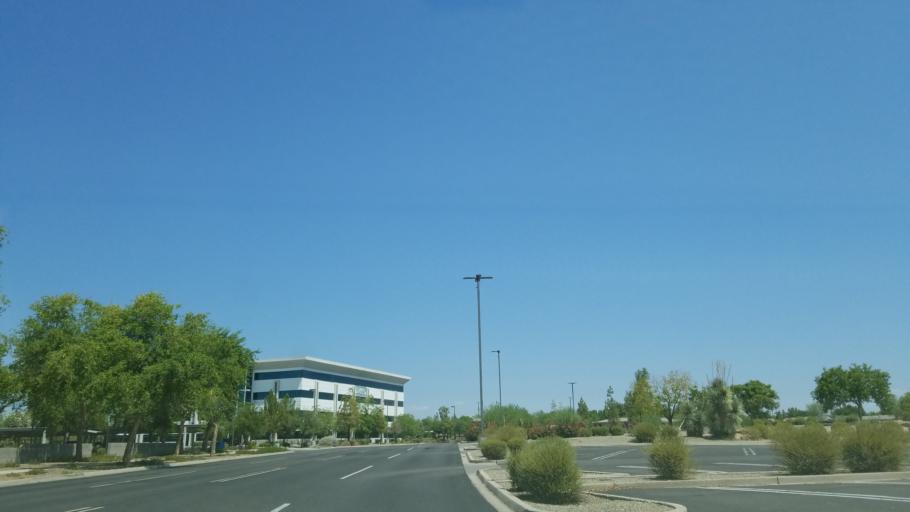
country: US
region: Arizona
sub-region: Maricopa County
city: Sun City
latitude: 33.6438
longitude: -112.2290
